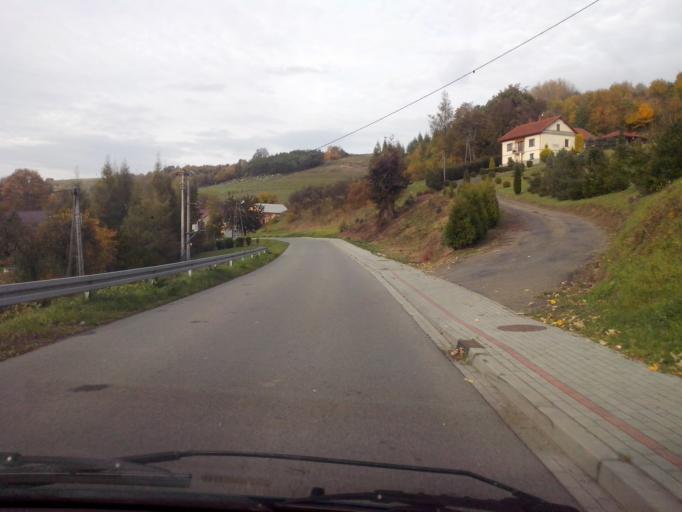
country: PL
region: Subcarpathian Voivodeship
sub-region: Powiat strzyzowski
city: Wisniowa
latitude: 49.8853
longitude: 21.6699
